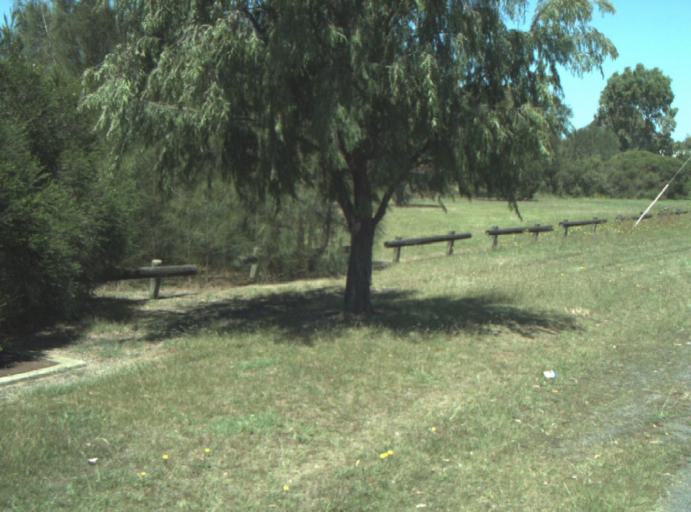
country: AU
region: Victoria
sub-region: Queenscliffe
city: Queenscliff
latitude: -38.1747
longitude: 144.7086
